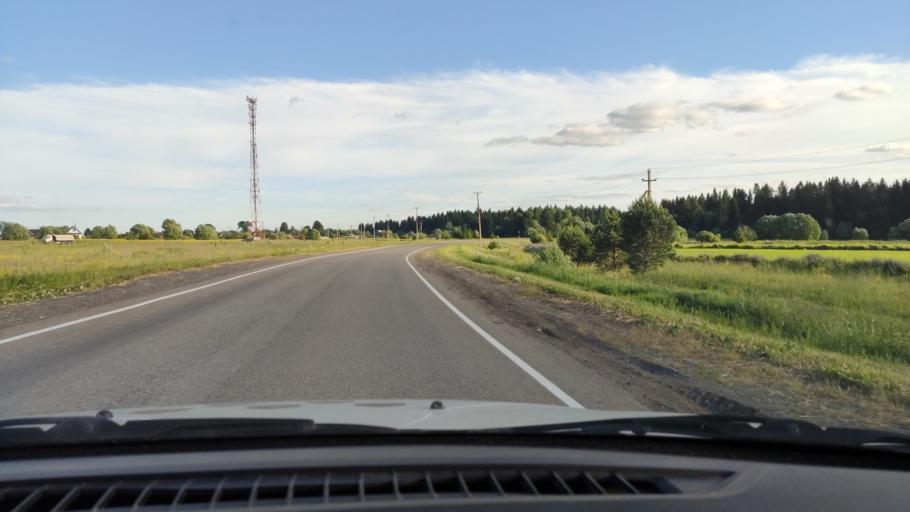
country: RU
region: Perm
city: Kungur
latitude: 57.4035
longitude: 56.8839
